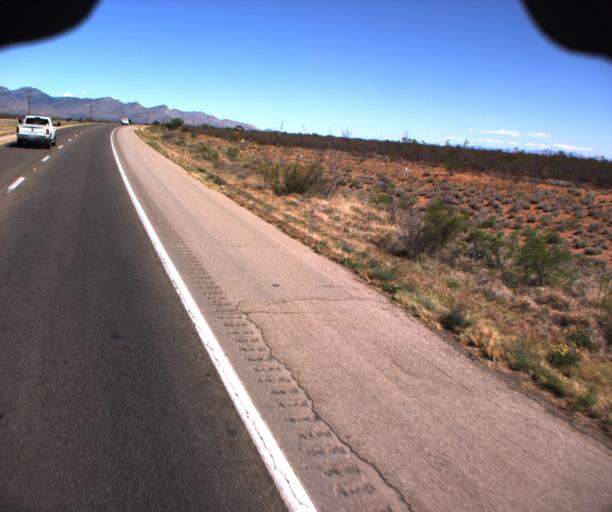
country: US
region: Arizona
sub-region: Cochise County
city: Huachuca City
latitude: 31.6603
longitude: -110.3493
